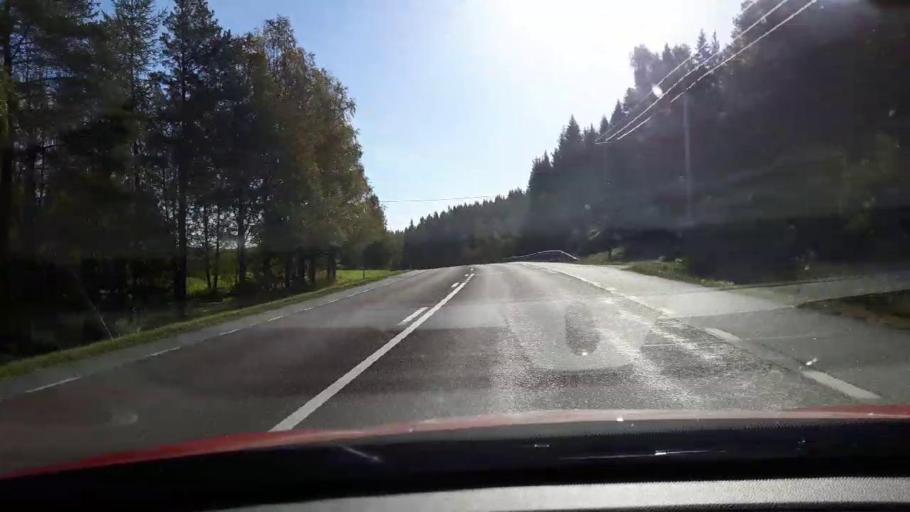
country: SE
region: Jaemtland
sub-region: OEstersunds Kommun
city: Brunflo
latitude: 62.9544
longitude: 15.1377
